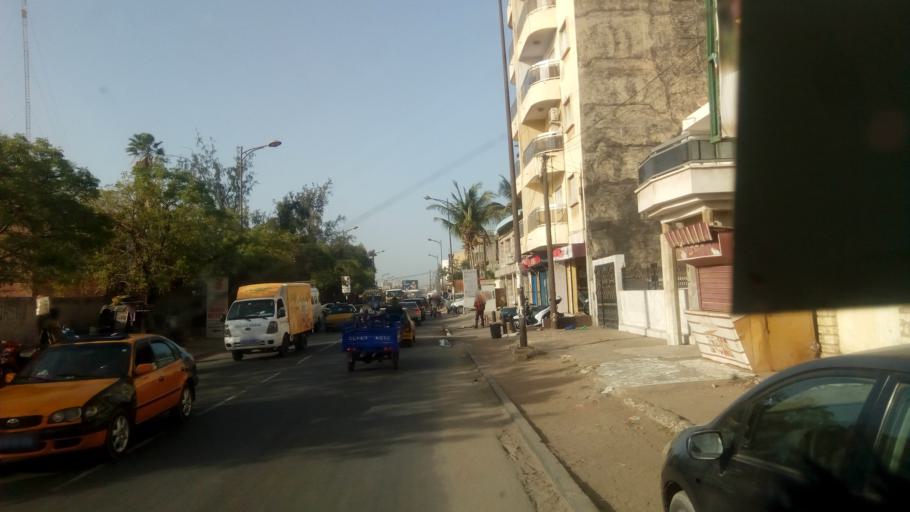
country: SN
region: Dakar
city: Dakar
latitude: 14.6966
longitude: -17.4473
